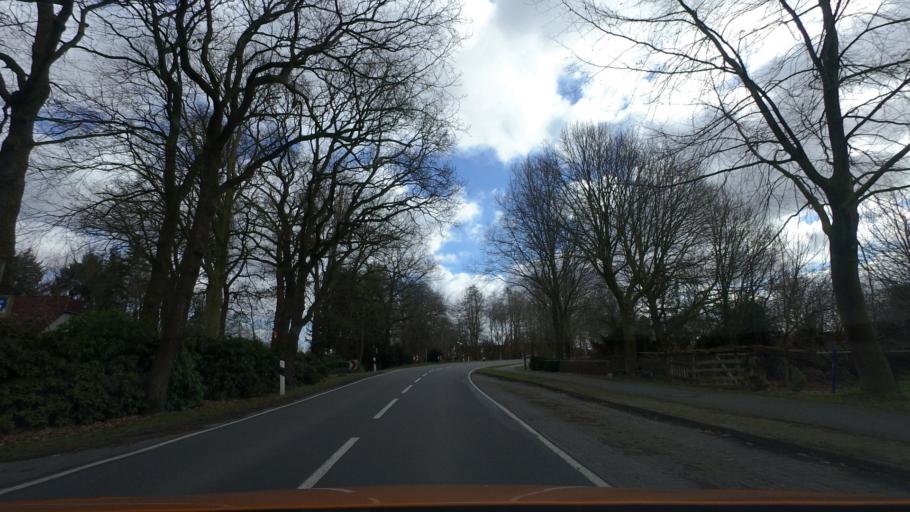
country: DE
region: Lower Saxony
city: Bad Zwischenahn
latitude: 53.1565
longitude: 8.0893
